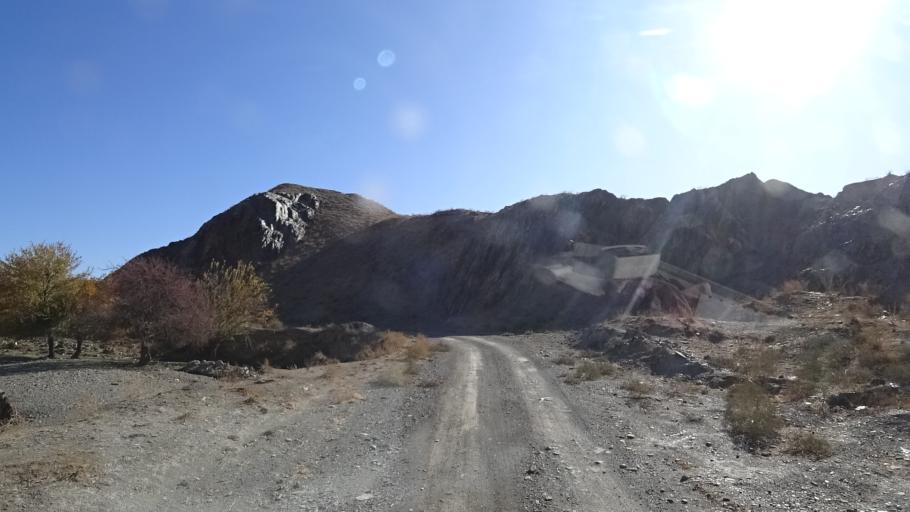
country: UZ
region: Navoiy
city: Nurota
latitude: 40.2985
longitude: 65.6062
